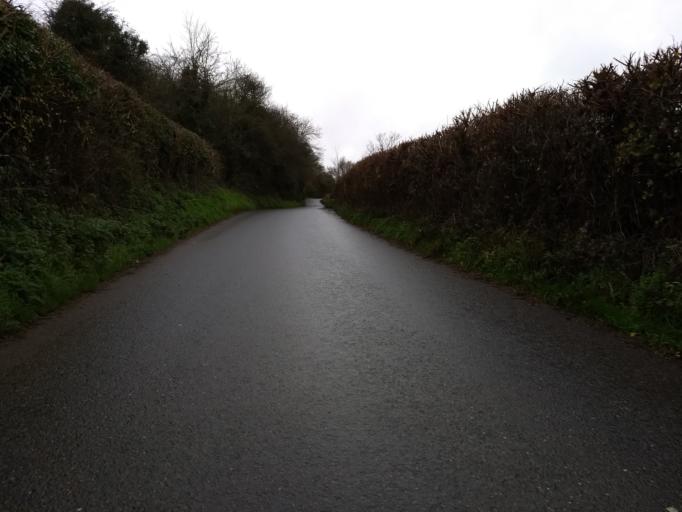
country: GB
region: England
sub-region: Isle of Wight
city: Newport
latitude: 50.6891
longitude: -1.2789
